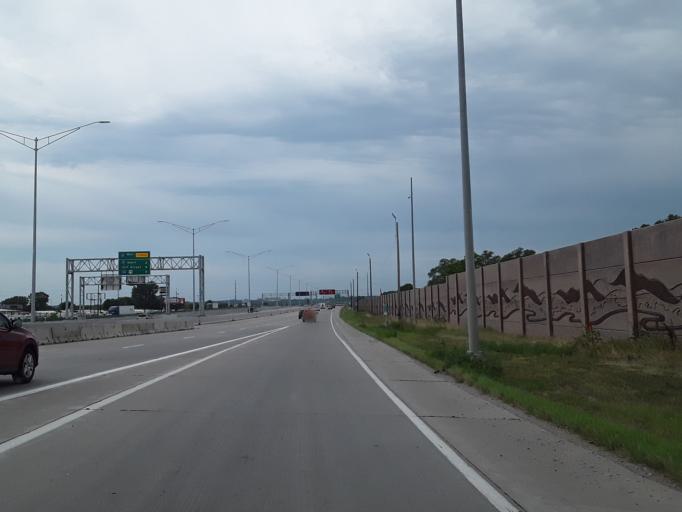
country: US
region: Iowa
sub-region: Pottawattamie County
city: Council Bluffs
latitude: 41.2327
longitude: -95.8575
